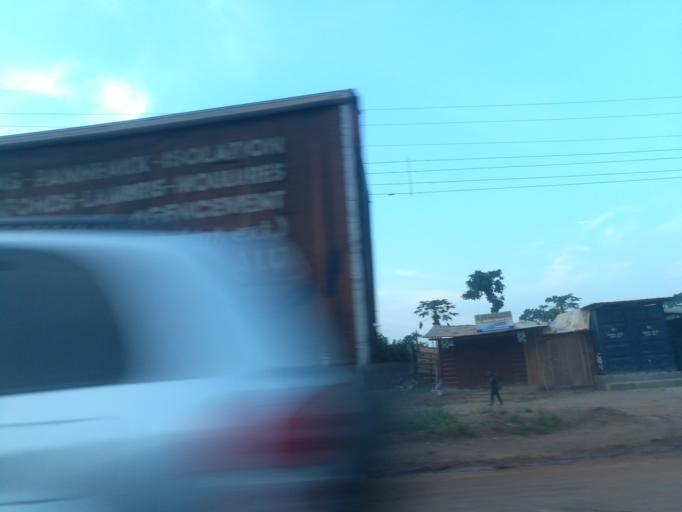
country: NG
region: Ogun
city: Abeokuta
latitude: 7.1773
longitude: 3.3909
